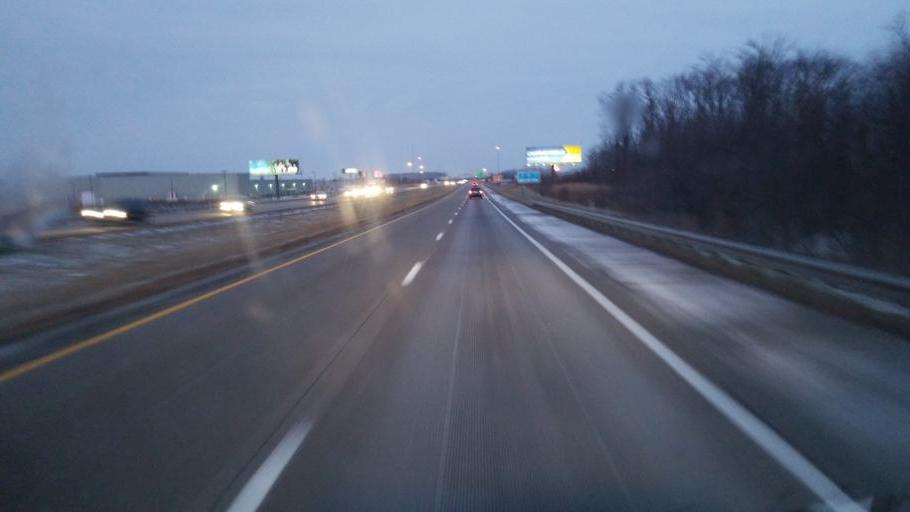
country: US
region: Indiana
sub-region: Wayne County
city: Richmond
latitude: 39.8694
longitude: -84.9138
